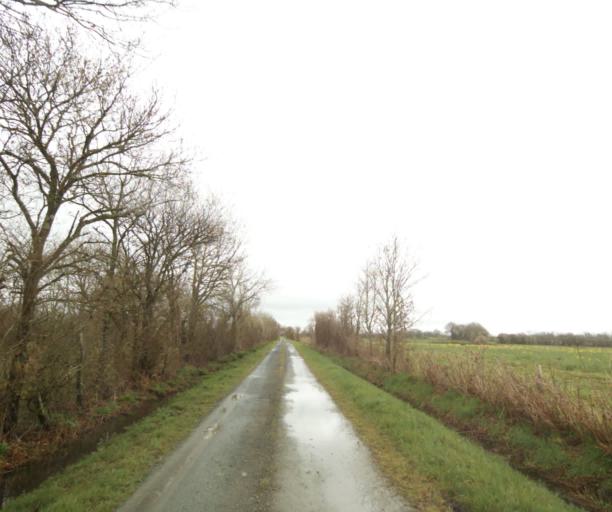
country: FR
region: Pays de la Loire
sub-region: Departement de la Loire-Atlantique
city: Bouvron
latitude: 47.4468
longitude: -1.8579
